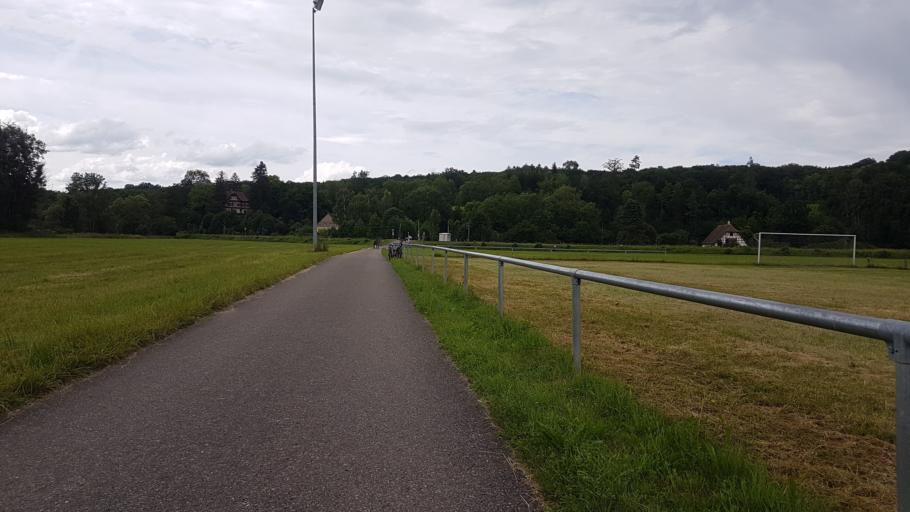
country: DE
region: Baden-Wuerttemberg
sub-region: Tuebingen Region
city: Obermarchtal
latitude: 48.2382
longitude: 9.5663
